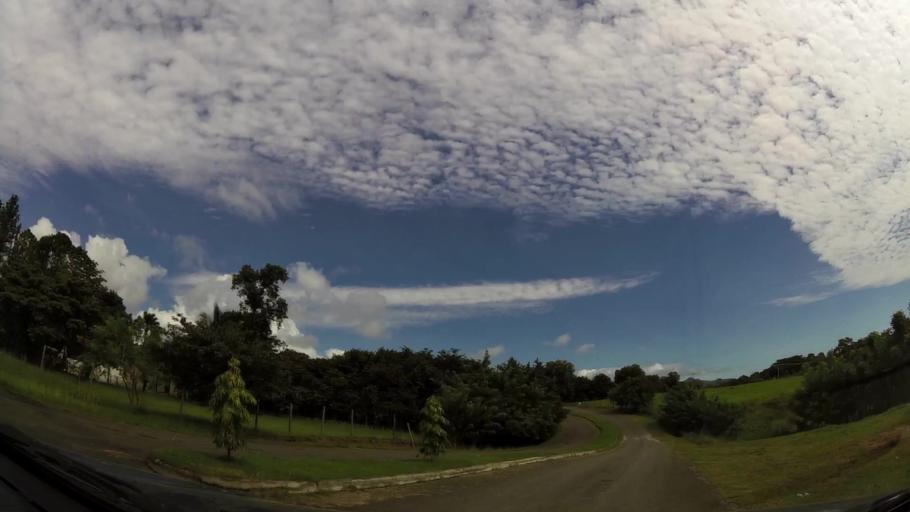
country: PA
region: Panama
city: Nueva Gorgona
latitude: 8.5368
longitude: -79.9085
